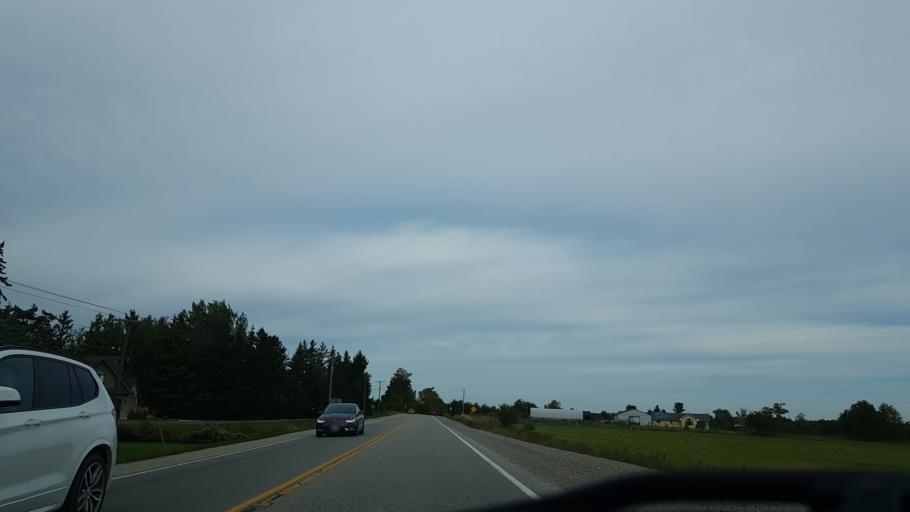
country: CA
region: Ontario
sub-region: Wellington County
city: Guelph
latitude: 43.6225
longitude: -80.2133
